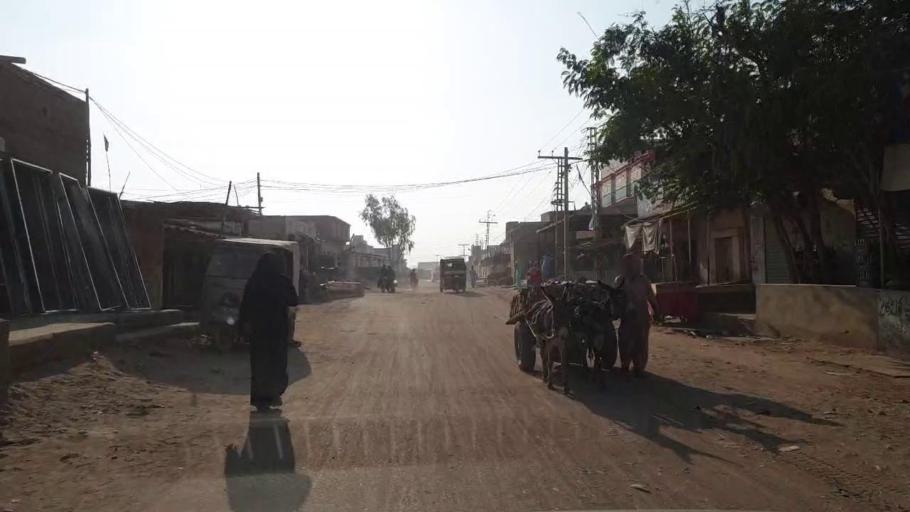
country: PK
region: Sindh
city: Kotri
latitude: 25.3548
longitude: 68.2660
